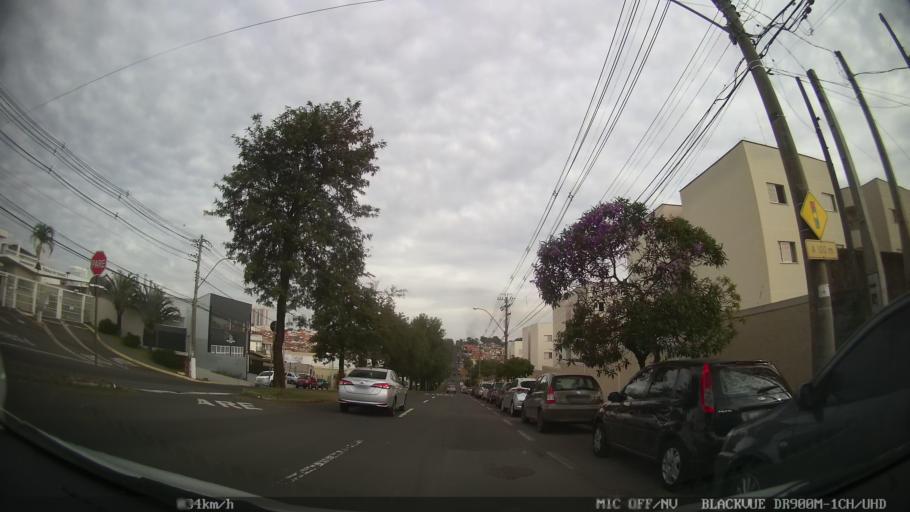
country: BR
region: Sao Paulo
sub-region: Piracicaba
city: Piracicaba
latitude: -22.7311
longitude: -47.6215
